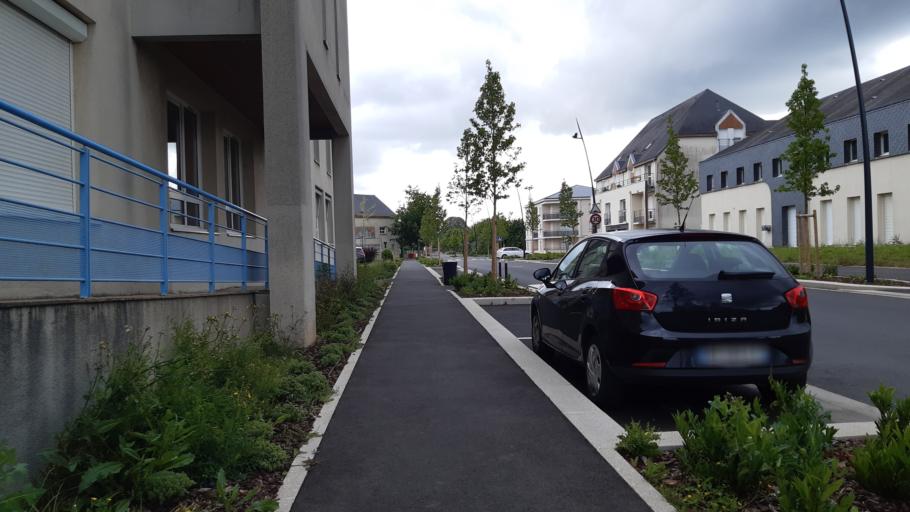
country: FR
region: Centre
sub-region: Departement d'Indre-et-Loire
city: Saint-Cyr-sur-Loire
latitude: 47.4231
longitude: 0.6677
